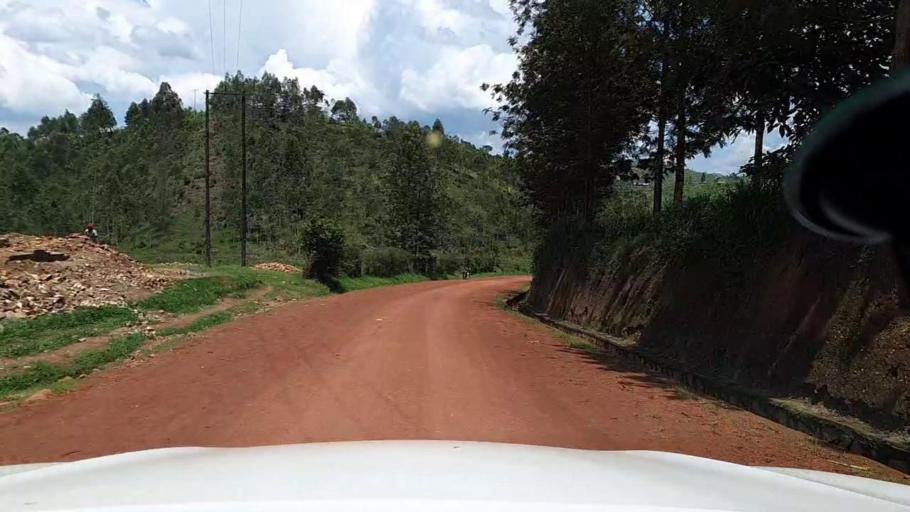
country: RW
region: Northern Province
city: Byumba
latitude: -1.7030
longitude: 29.8367
